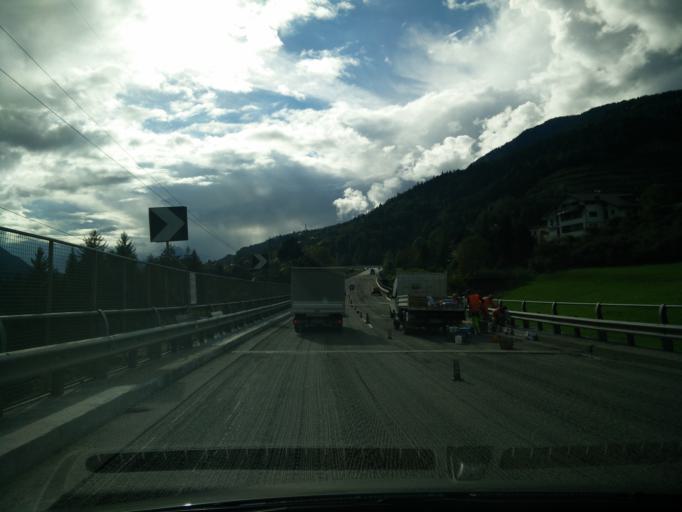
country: IT
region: Veneto
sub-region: Provincia di Belluno
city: Lozzo di Cadore
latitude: 46.4845
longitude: 12.4490
